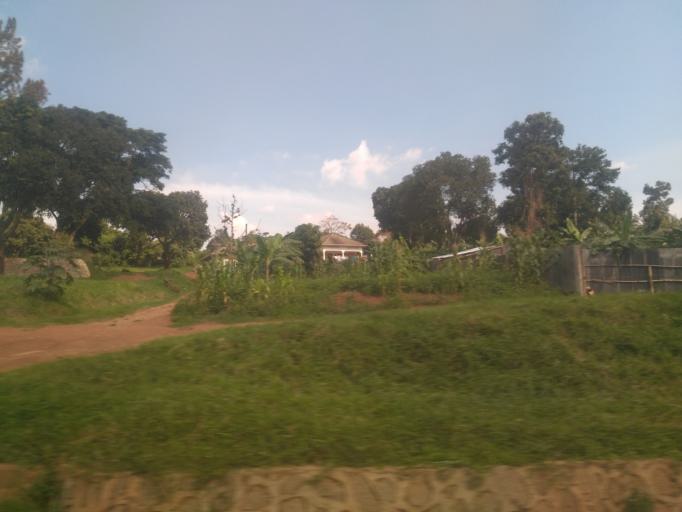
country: UG
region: Central Region
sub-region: Wakiso District
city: Kajansi
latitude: 0.2765
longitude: 32.4683
